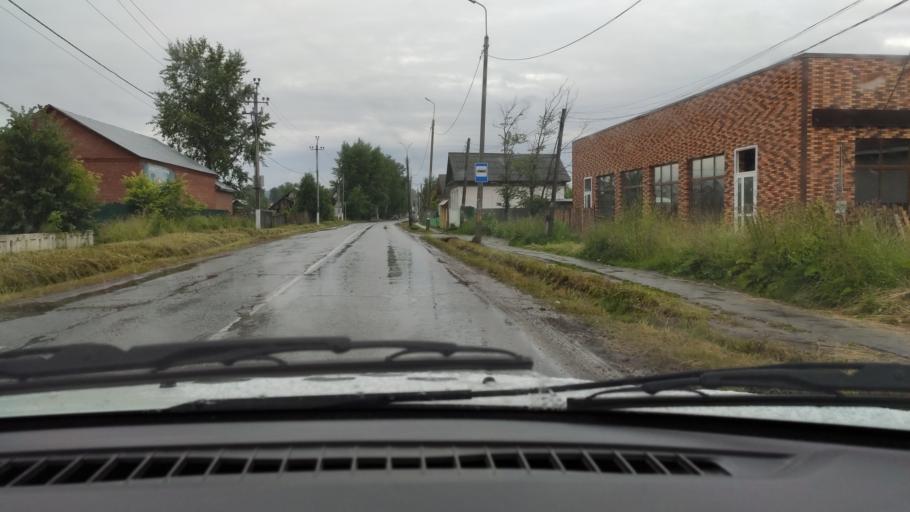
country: RU
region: Udmurtiya
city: Votkinsk
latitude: 57.0489
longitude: 53.9650
